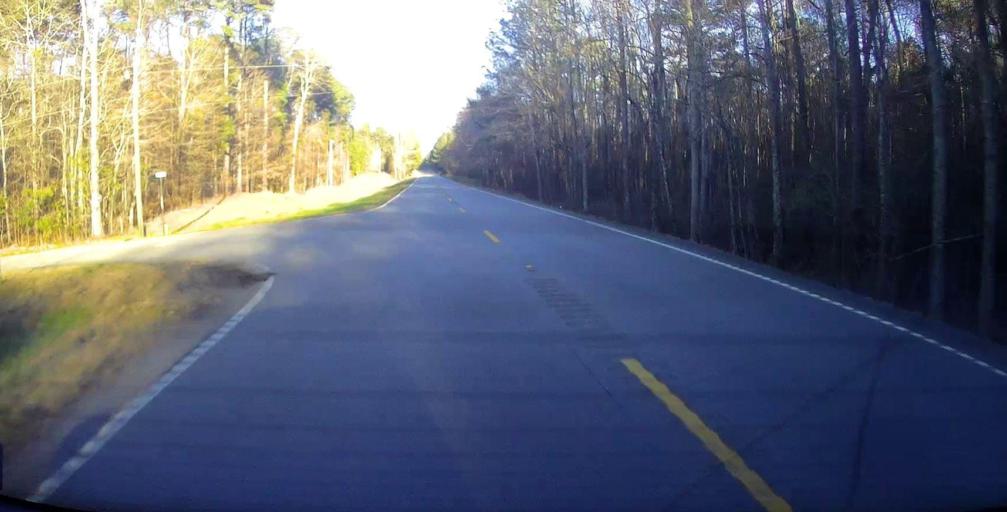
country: US
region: Georgia
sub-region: Harris County
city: Hamilton
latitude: 32.6323
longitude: -84.7406
